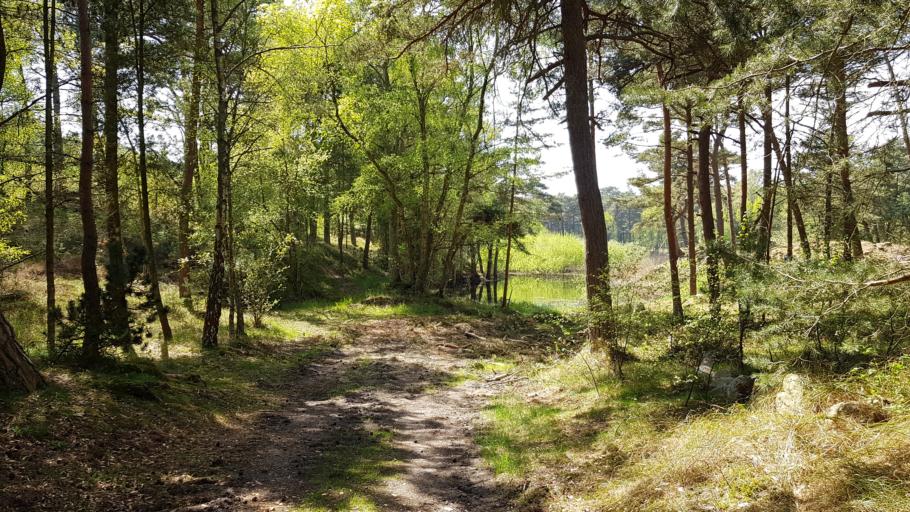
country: DK
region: Capital Region
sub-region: Bornholm Kommune
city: Nexo
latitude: 55.0000
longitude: 15.0911
